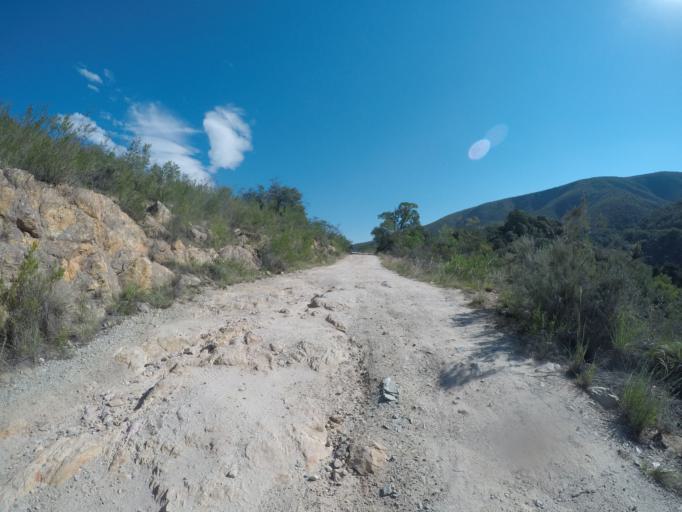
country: ZA
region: Eastern Cape
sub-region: Cacadu District Municipality
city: Kareedouw
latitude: -33.6467
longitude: 24.4622
